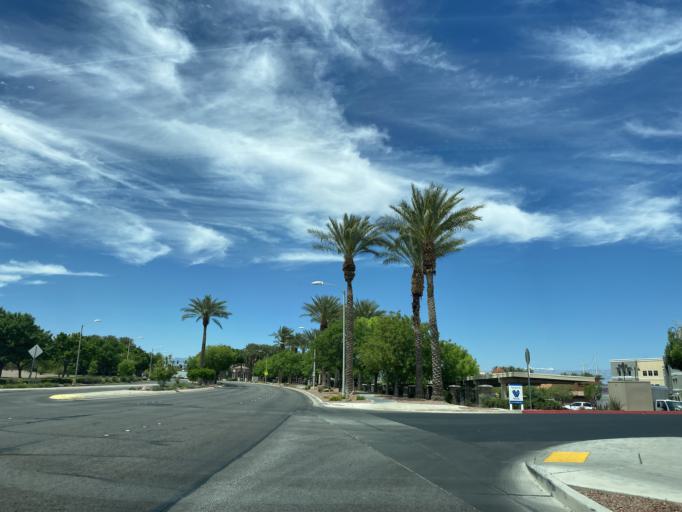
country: US
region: Nevada
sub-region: Clark County
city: Whitney
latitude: 36.0209
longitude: -115.0808
